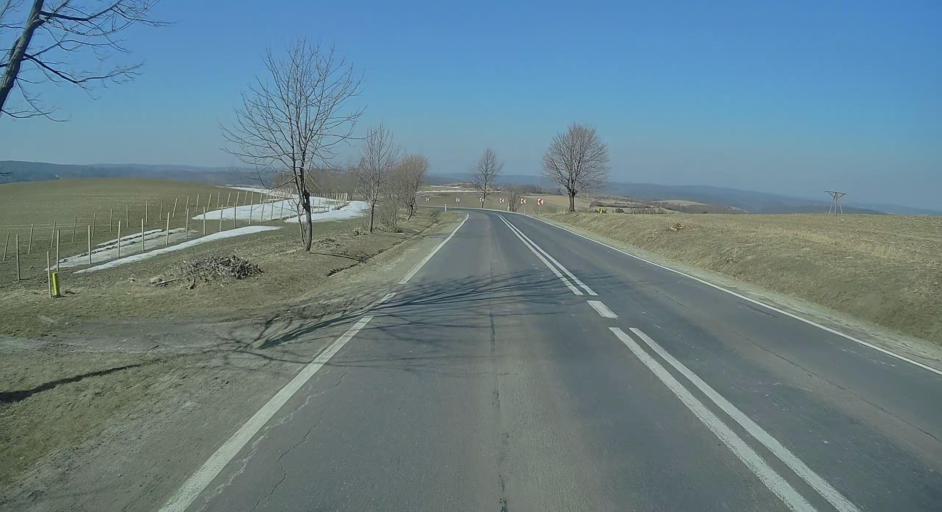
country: PL
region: Subcarpathian Voivodeship
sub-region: Powiat sanocki
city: Tyrawa Woloska
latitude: 49.6313
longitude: 22.4273
